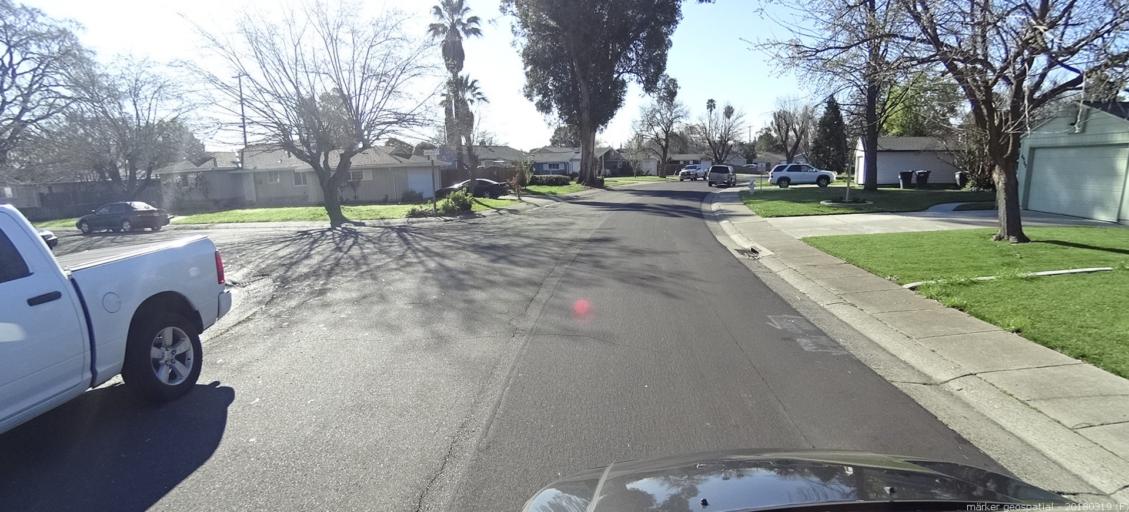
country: US
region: California
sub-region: Sacramento County
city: Parkway
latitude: 38.4897
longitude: -121.4454
